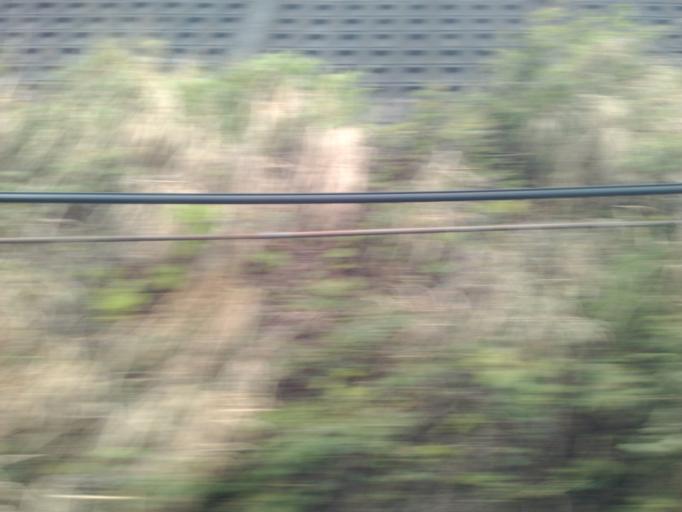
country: JP
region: Kanagawa
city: Yokohama
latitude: 35.4832
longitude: 139.5789
